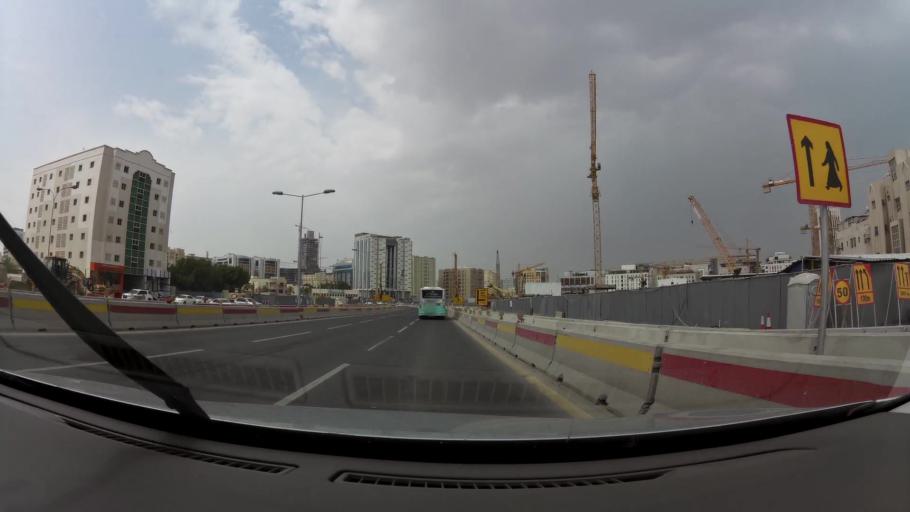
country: QA
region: Baladiyat ad Dawhah
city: Doha
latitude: 25.2809
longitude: 51.5262
